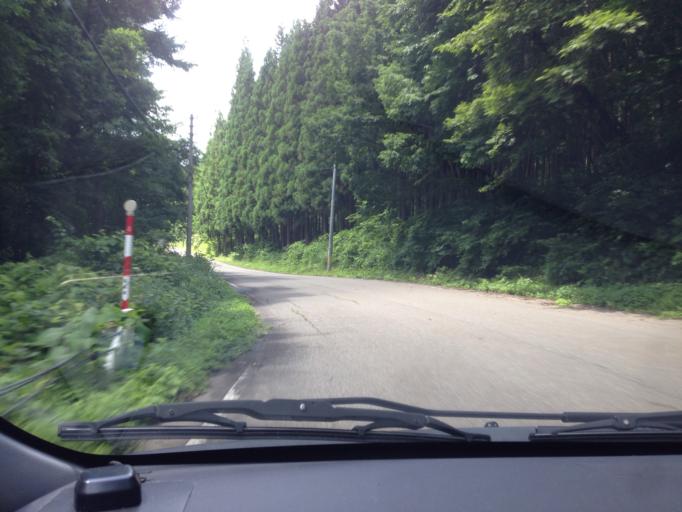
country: JP
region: Fukushima
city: Kitakata
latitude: 37.3044
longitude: 139.8467
